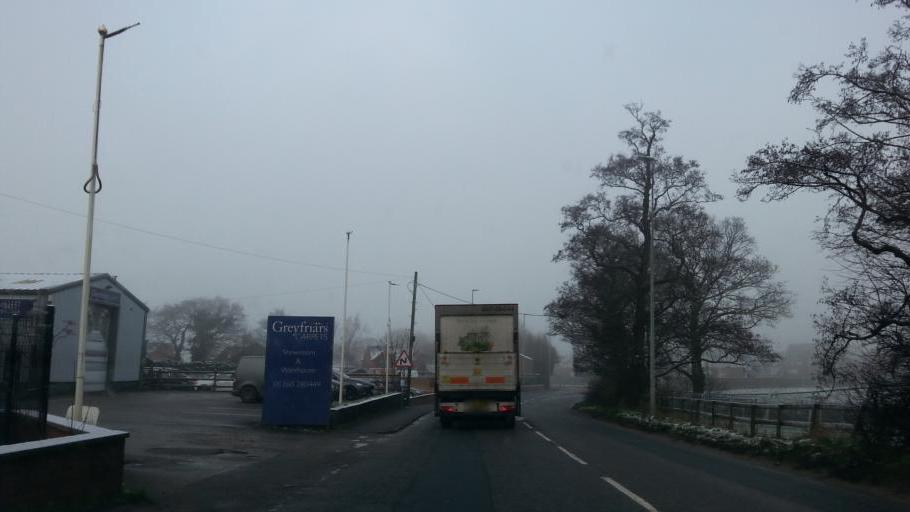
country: GB
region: England
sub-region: Cheshire East
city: Eaton
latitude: 53.1776
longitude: -2.2097
